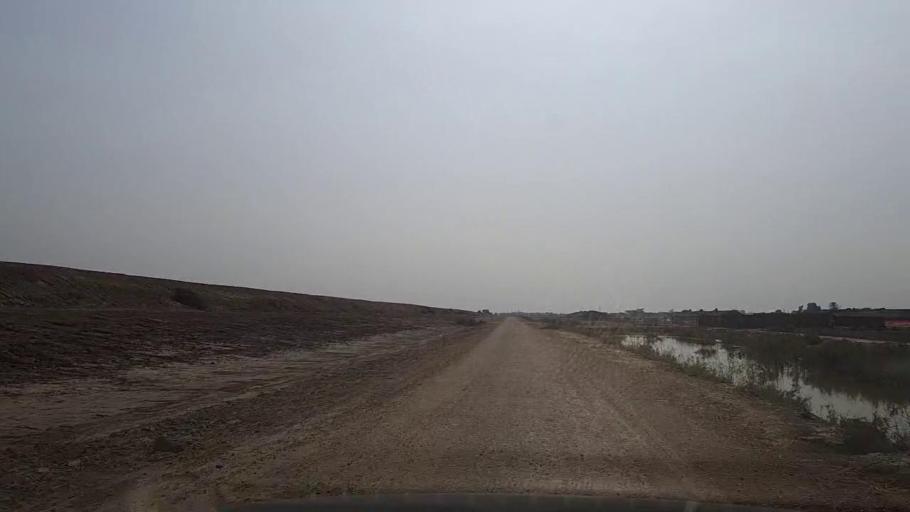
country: PK
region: Sindh
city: Thatta
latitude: 24.5685
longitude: 67.9133
